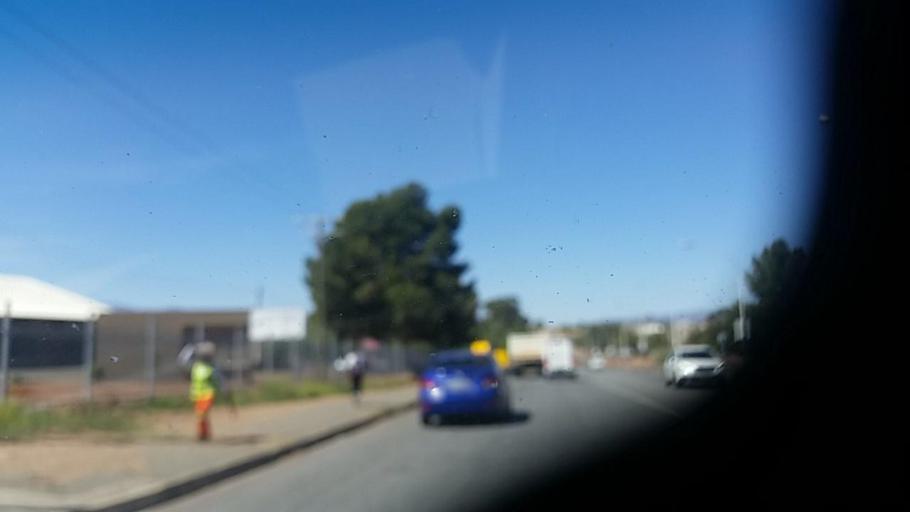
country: ZA
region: Western Cape
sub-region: Eden District Municipality
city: Oudtshoorn
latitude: -33.5946
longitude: 22.2194
